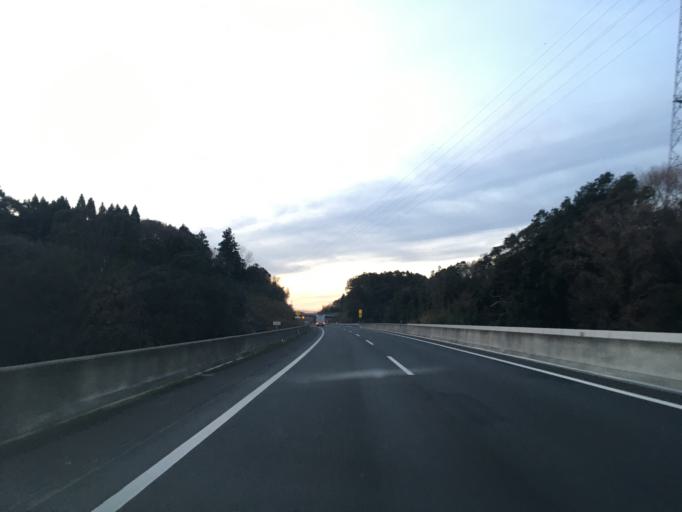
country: JP
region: Ibaraki
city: Inashiki
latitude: 35.9360
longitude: 140.3371
